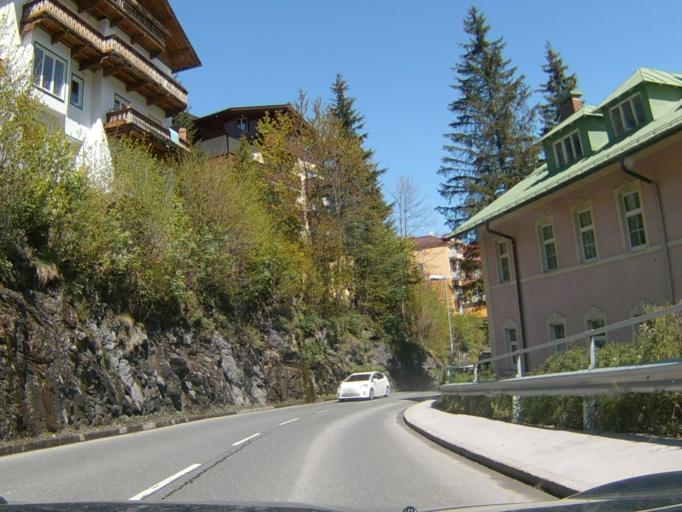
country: AT
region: Salzburg
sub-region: Politischer Bezirk Sankt Johann im Pongau
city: Bad Gastein
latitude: 47.1174
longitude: 13.1337
